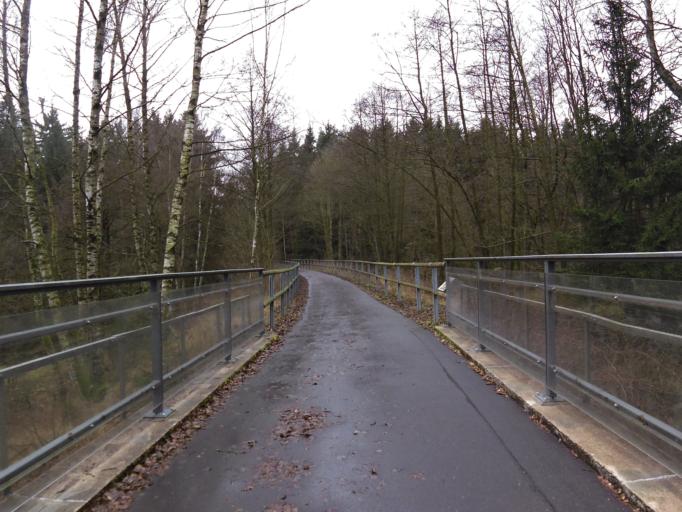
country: DE
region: Bavaria
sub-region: Upper Franconia
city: Wunsiedel
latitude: 50.0585
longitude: 12.0320
